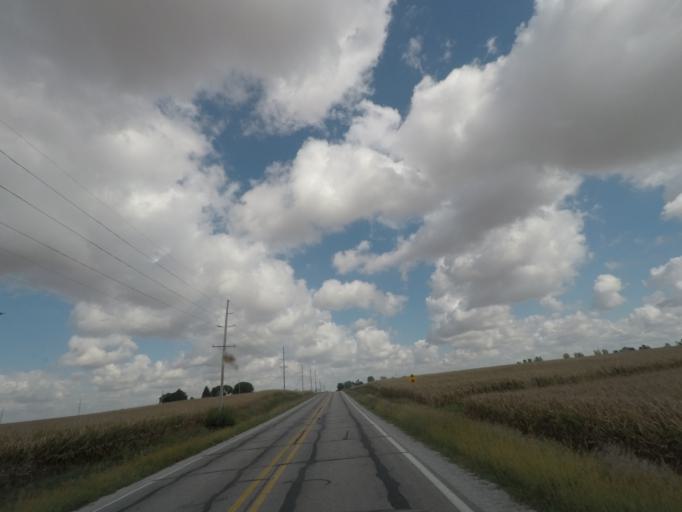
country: US
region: Iowa
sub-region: Story County
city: Nevada
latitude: 42.0199
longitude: -93.4057
